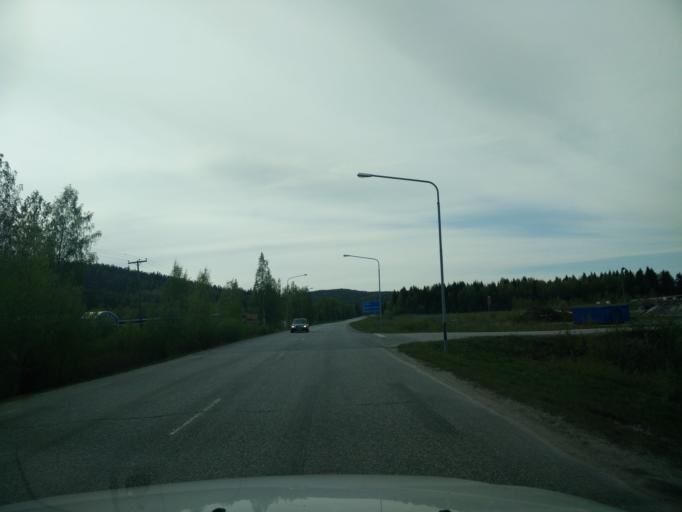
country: SE
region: Vaesternorrland
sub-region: OErnskoeldsviks Kommun
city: Bjasta
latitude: 63.2021
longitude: 18.4917
